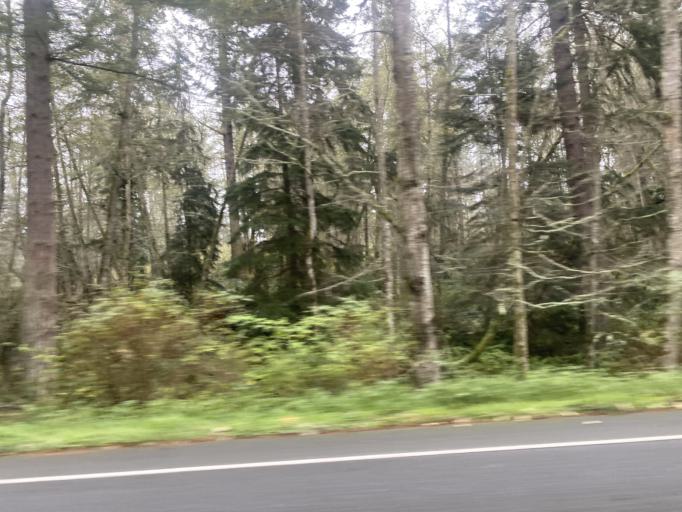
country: US
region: Washington
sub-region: Island County
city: Freeland
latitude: 48.0529
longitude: -122.5067
